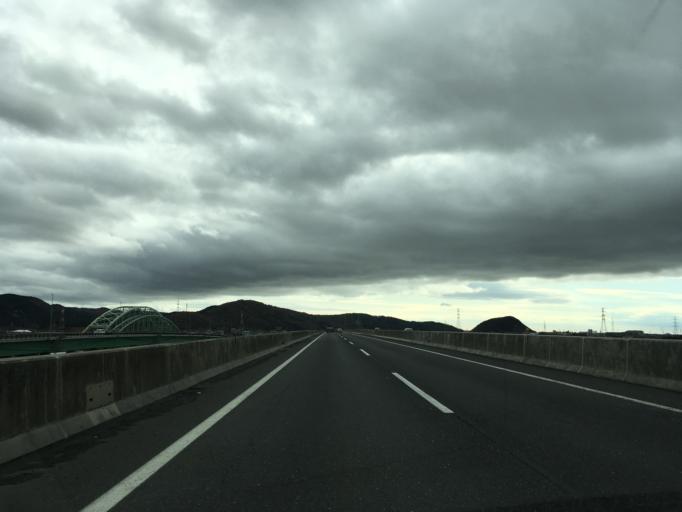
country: JP
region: Miyagi
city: Ishinomaki
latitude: 38.4949
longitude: 141.2886
